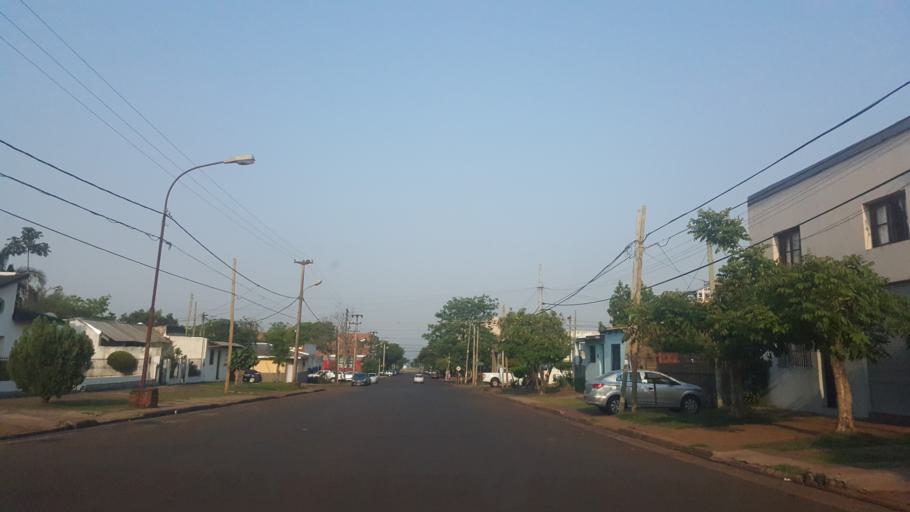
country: AR
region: Misiones
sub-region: Departamento de Capital
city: Posadas
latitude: -27.3946
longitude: -55.8989
